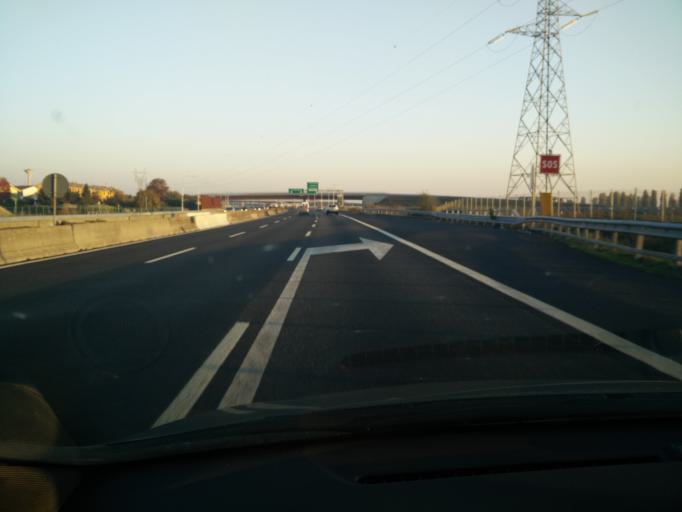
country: IT
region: Lombardy
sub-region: Citta metropolitana di Milano
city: Riozzo
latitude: 45.3432
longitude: 9.3172
